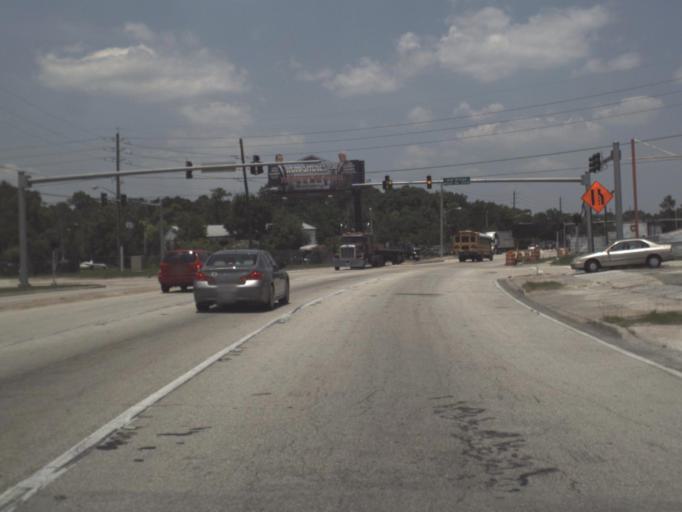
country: US
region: Florida
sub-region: Duval County
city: Jacksonville
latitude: 30.3613
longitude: -81.7311
